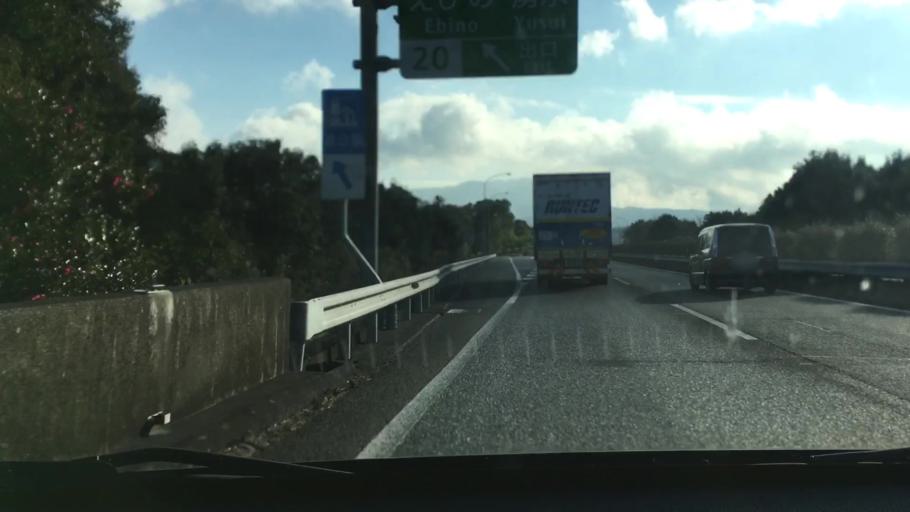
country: JP
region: Kumamoto
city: Hitoyoshi
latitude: 32.0528
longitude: 130.8019
